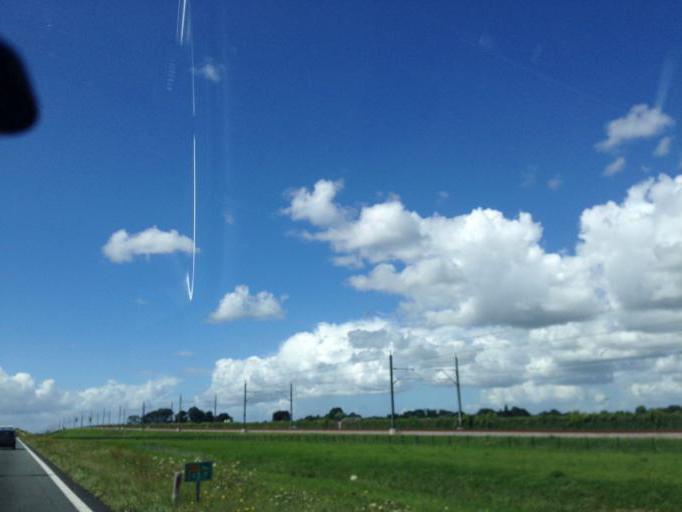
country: NL
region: Overijssel
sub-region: Gemeente Kampen
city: Kampen
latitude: 52.5066
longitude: 5.9682
